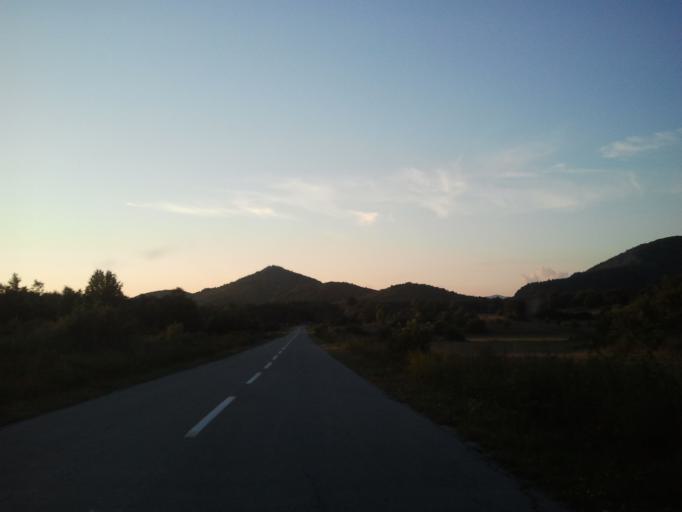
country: HR
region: Zadarska
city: Obrovac
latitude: 44.4168
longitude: 15.6634
